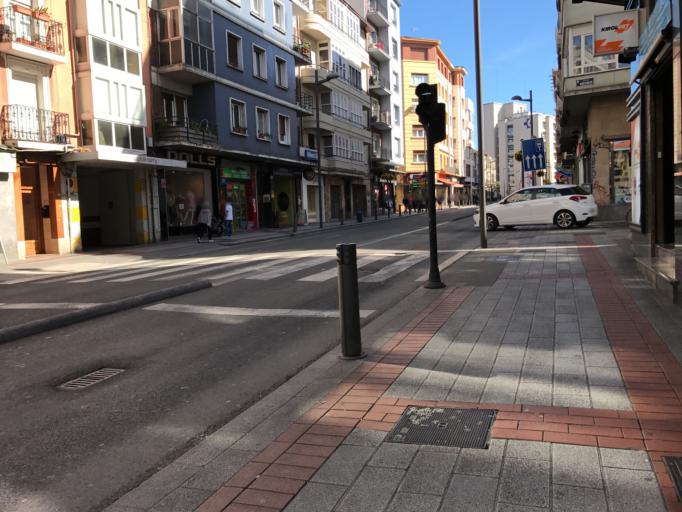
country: ES
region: Basque Country
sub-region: Provincia de Alava
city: Gasteiz / Vitoria
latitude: 42.8484
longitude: -2.6683
